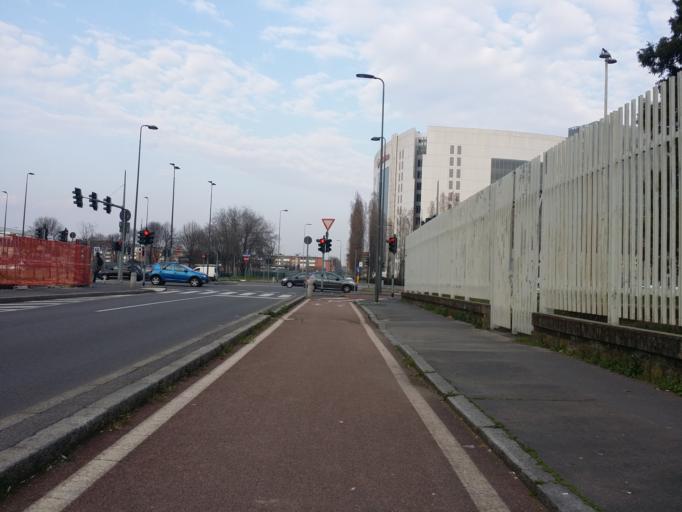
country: IT
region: Lombardy
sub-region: Citta metropolitana di Milano
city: Romano Banco
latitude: 45.4468
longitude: 9.1197
